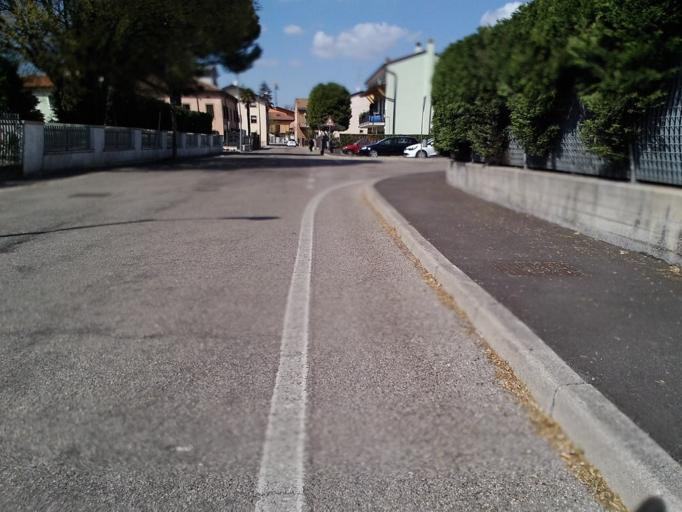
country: IT
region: Veneto
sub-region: Provincia di Verona
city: Dossobuono
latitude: 45.4051
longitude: 10.9305
